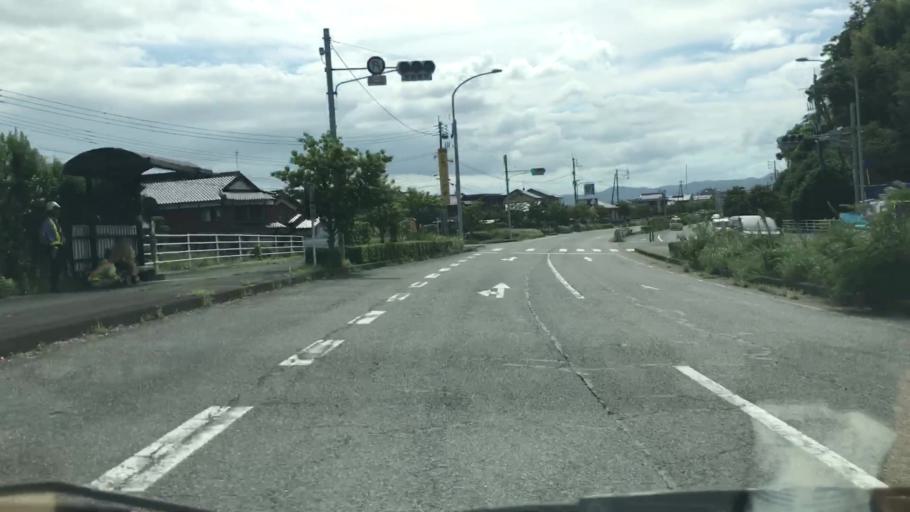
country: JP
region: Saga Prefecture
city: Saga-shi
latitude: 33.2268
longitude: 130.1792
